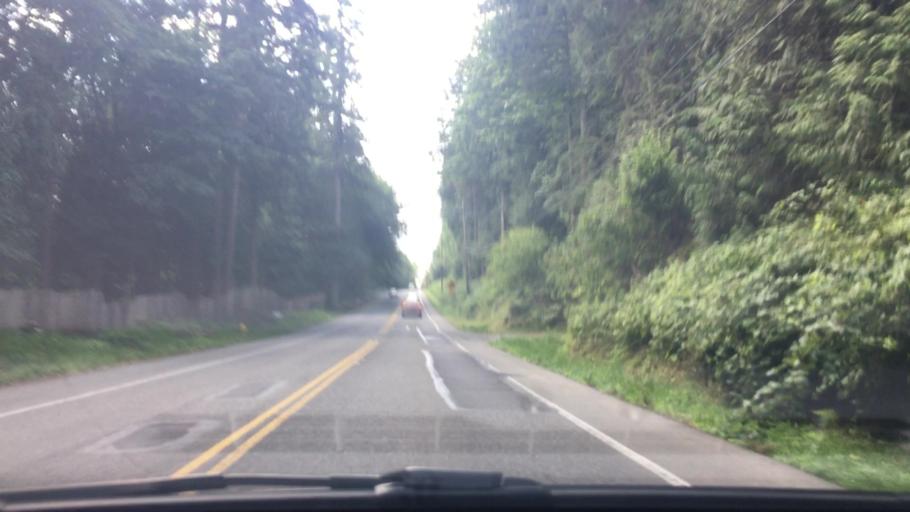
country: US
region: Washington
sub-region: King County
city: City of Sammamish
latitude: 47.5726
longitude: -122.0358
